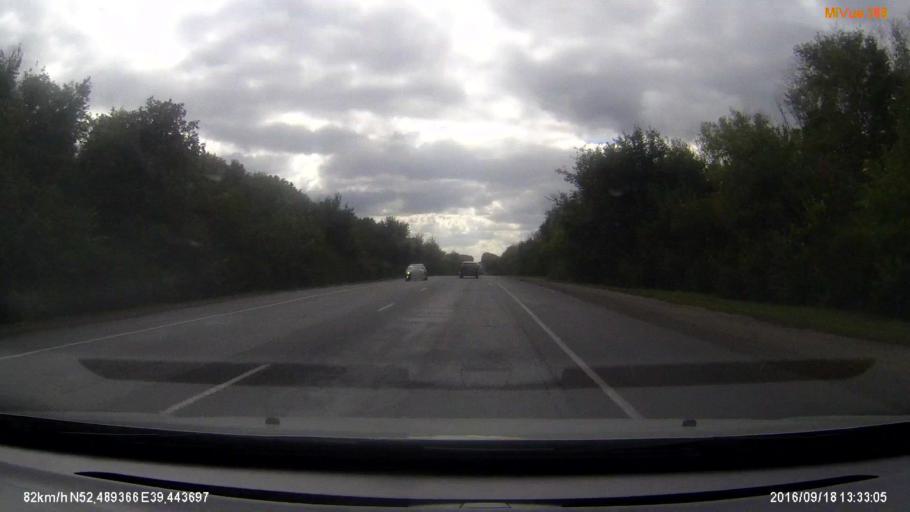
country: RU
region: Lipetsk
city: Borinskoye
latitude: 52.4747
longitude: 39.4253
